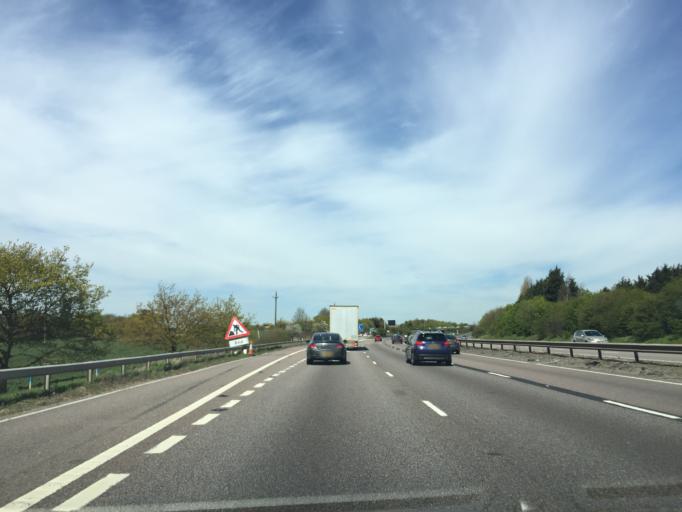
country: GB
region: England
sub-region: Essex
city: Epping
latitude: 51.7370
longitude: 0.1367
